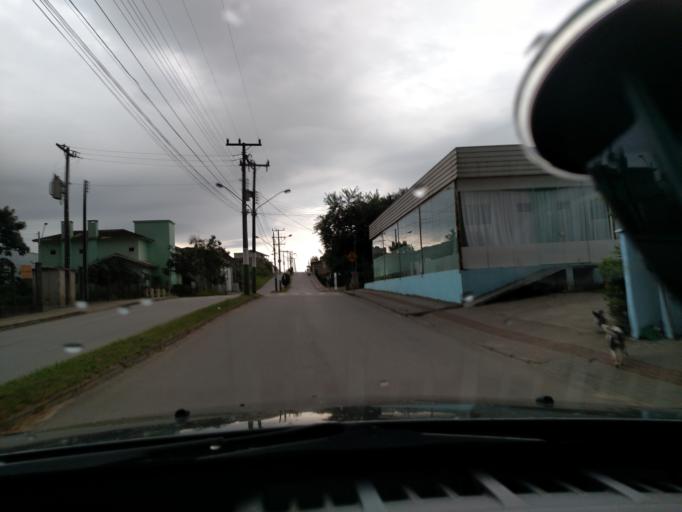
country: BR
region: Santa Catarina
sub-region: Brusque
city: Brusque
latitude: -27.0778
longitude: -48.9162
